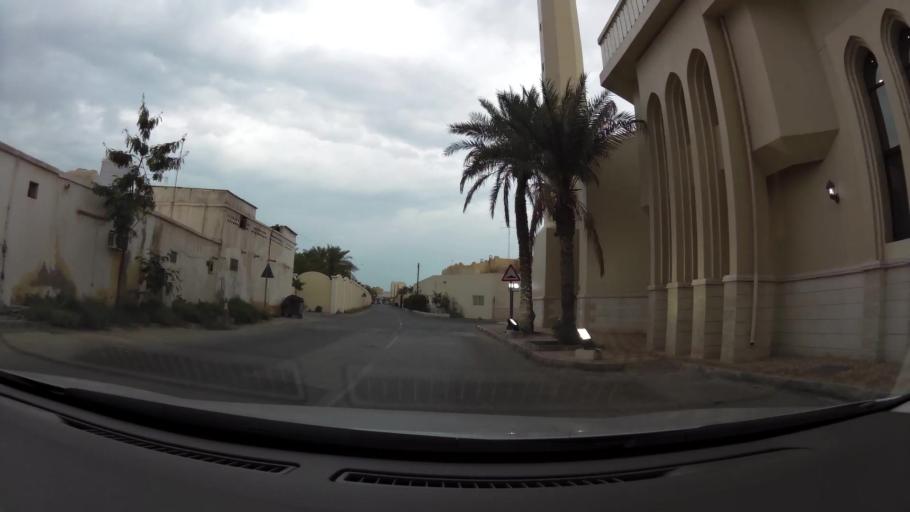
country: QA
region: Baladiyat ad Dawhah
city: Doha
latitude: 25.2705
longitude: 51.5021
